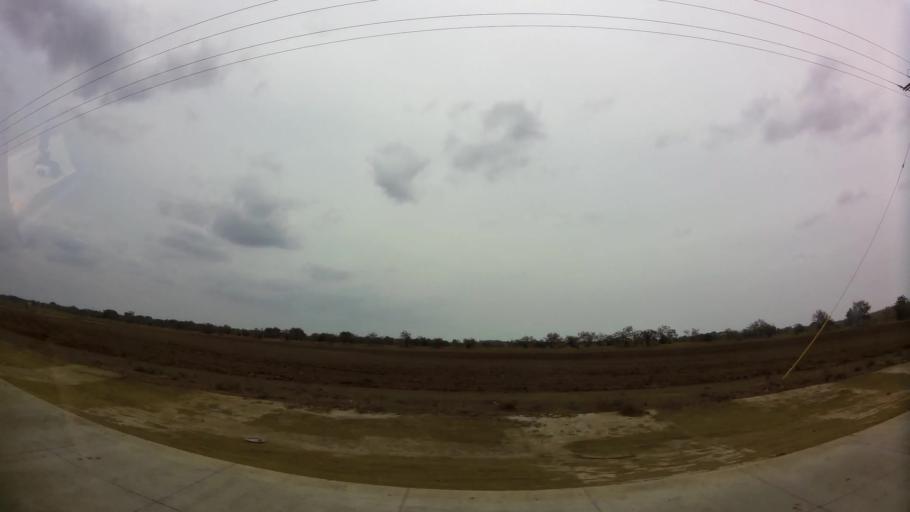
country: NI
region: Managua
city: Managua
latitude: 12.1088
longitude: -86.1736
